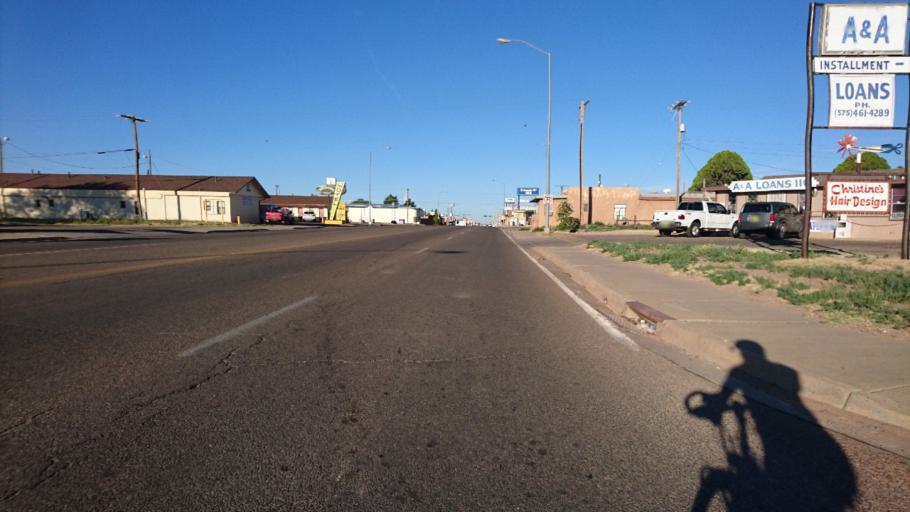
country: US
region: New Mexico
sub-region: Quay County
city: Tucumcari
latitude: 35.1719
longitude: -103.7211
